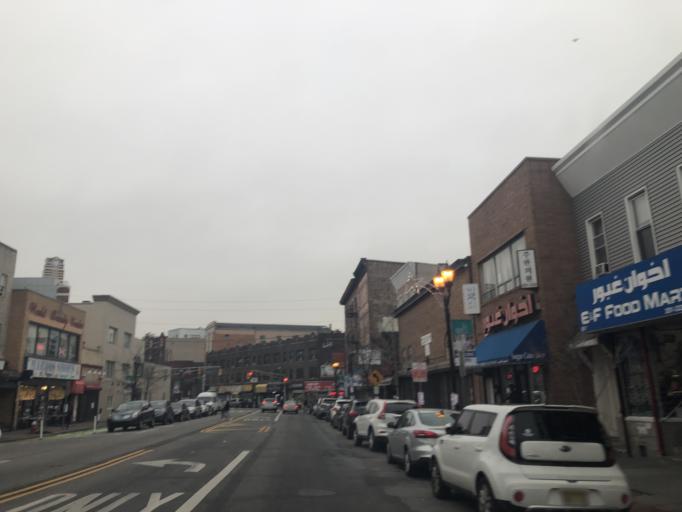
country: US
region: New Jersey
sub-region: Hudson County
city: Jersey City
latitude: 40.7294
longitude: -74.0664
